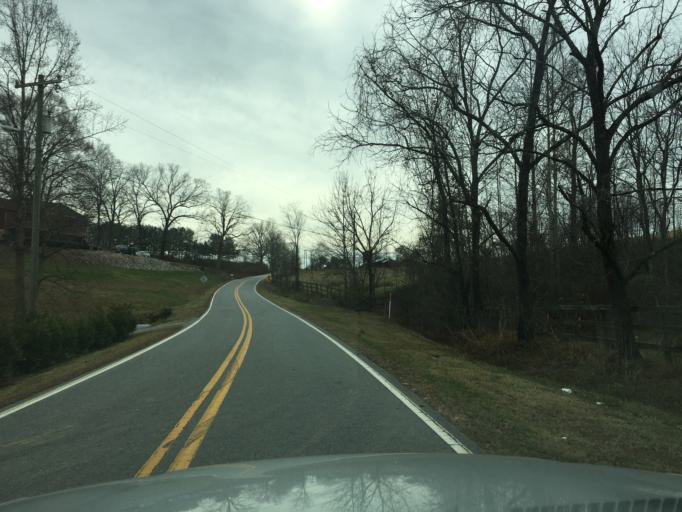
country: US
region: North Carolina
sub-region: McDowell County
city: West Marion
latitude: 35.6302
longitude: -81.9658
